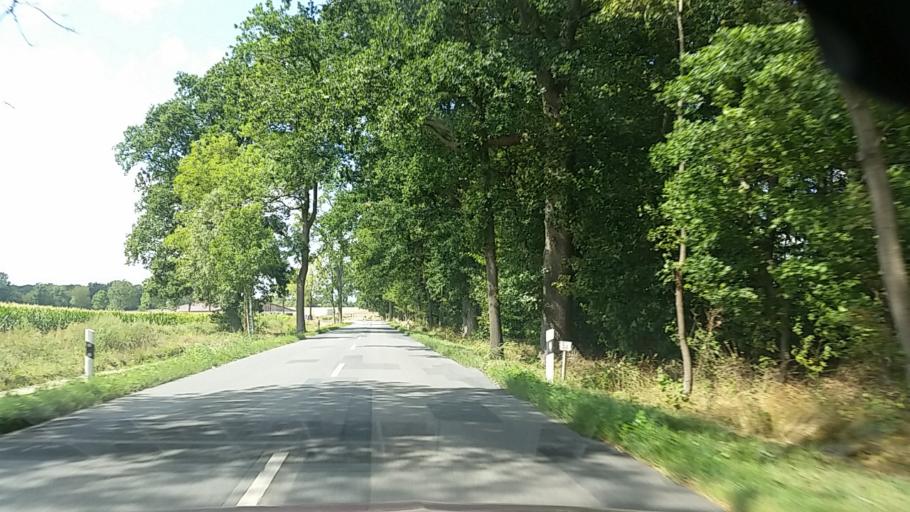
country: DE
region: Lower Saxony
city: Hankensbuttel
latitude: 52.7082
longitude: 10.6398
